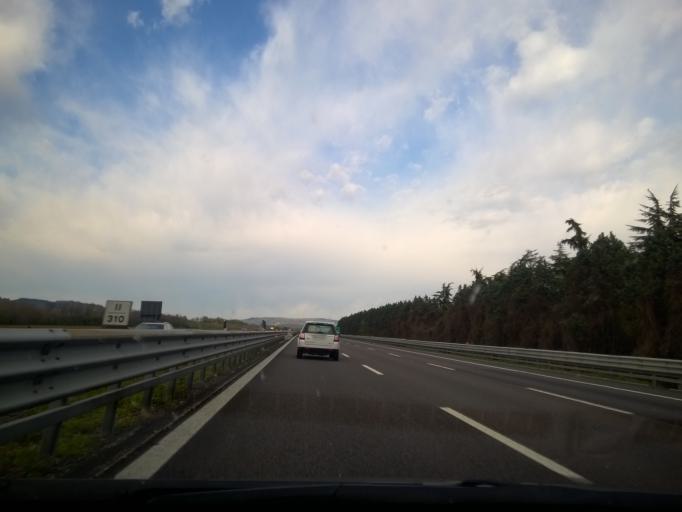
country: IT
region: Veneto
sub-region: Provincia di Verona
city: Locara
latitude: 45.4287
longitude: 11.3384
